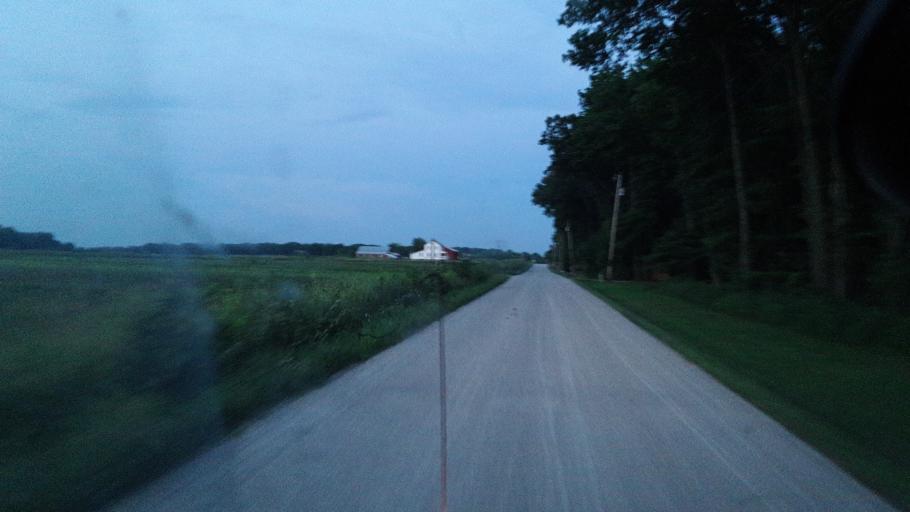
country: US
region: Ohio
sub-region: Wayne County
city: West Salem
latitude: 41.0136
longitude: -82.1925
